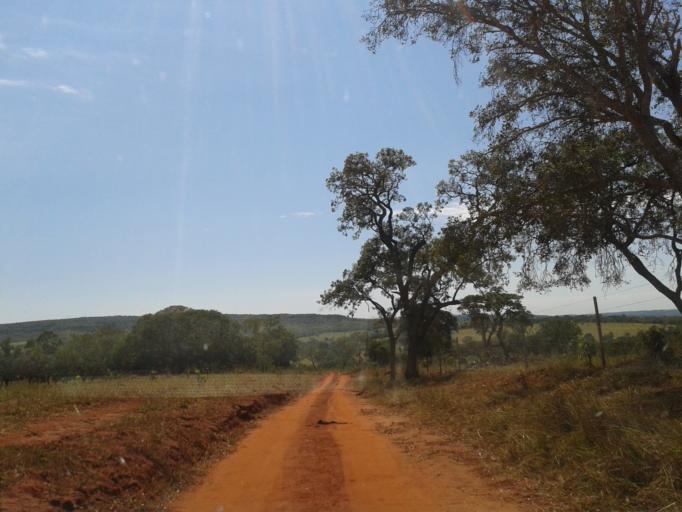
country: BR
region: Minas Gerais
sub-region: Campina Verde
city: Campina Verde
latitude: -19.3975
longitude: -49.7659
